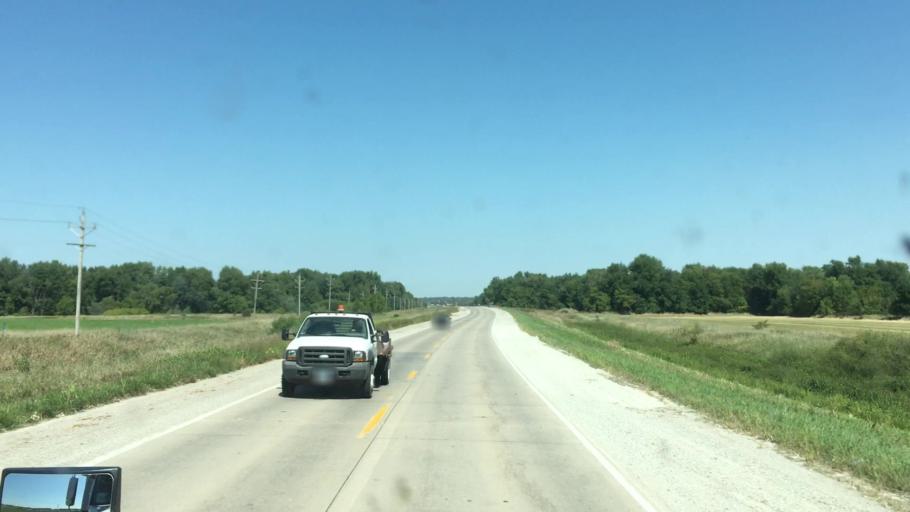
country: US
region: Iowa
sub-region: Benton County
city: Belle Plaine
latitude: 41.8552
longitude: -92.2783
